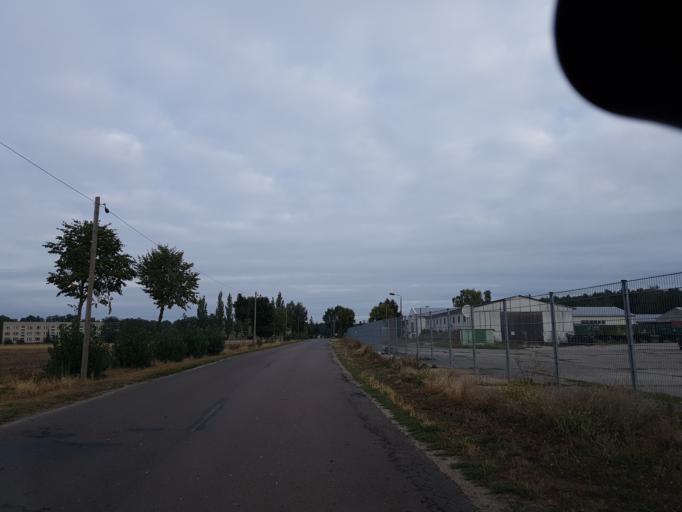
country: DE
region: Saxony-Anhalt
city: Klieken
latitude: 51.9497
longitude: 12.3108
